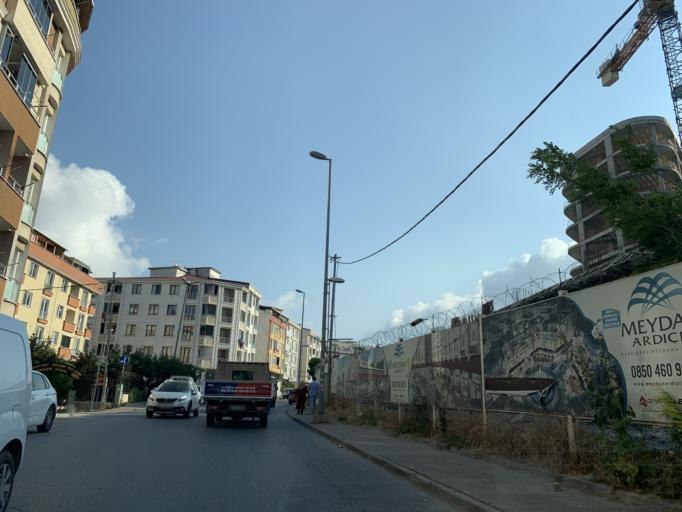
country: TR
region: Istanbul
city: Esenyurt
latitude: 41.0446
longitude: 28.6770
